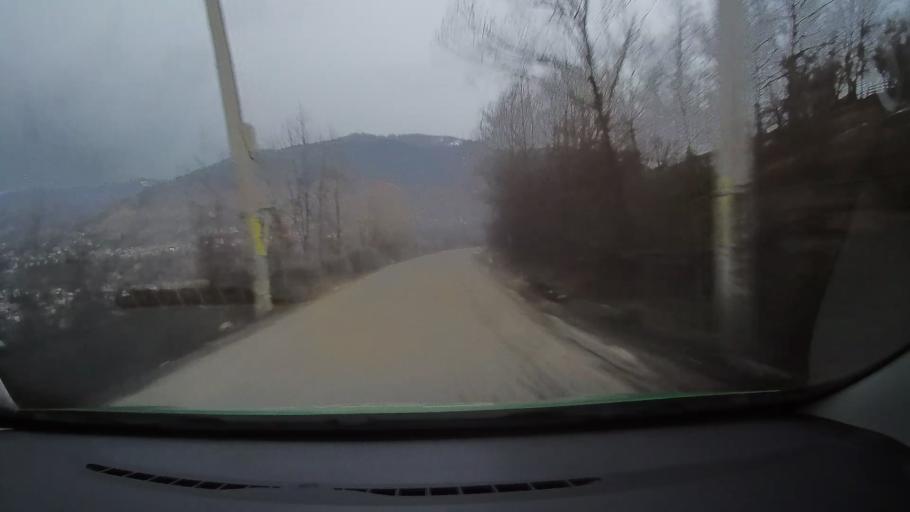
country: RO
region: Prahova
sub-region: Comuna Valea Doftanei
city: Tesila
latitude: 45.2969
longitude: 25.7157
